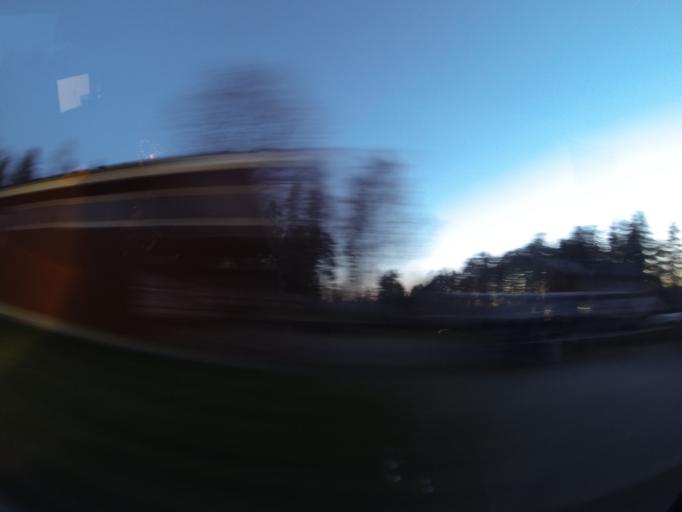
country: SE
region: OErebro
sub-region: Lindesbergs Kommun
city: Fellingsbro
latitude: 59.3724
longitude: 15.6552
